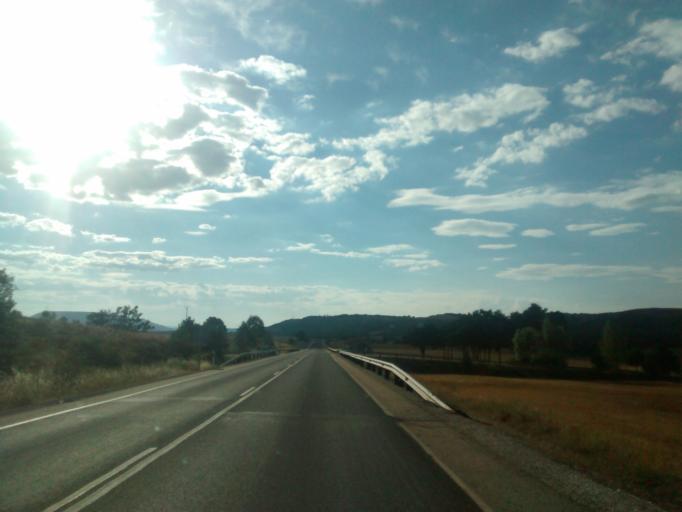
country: ES
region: Castille and Leon
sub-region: Provincia de Burgos
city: Basconcillos del Tozo
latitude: 42.6740
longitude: -3.9356
